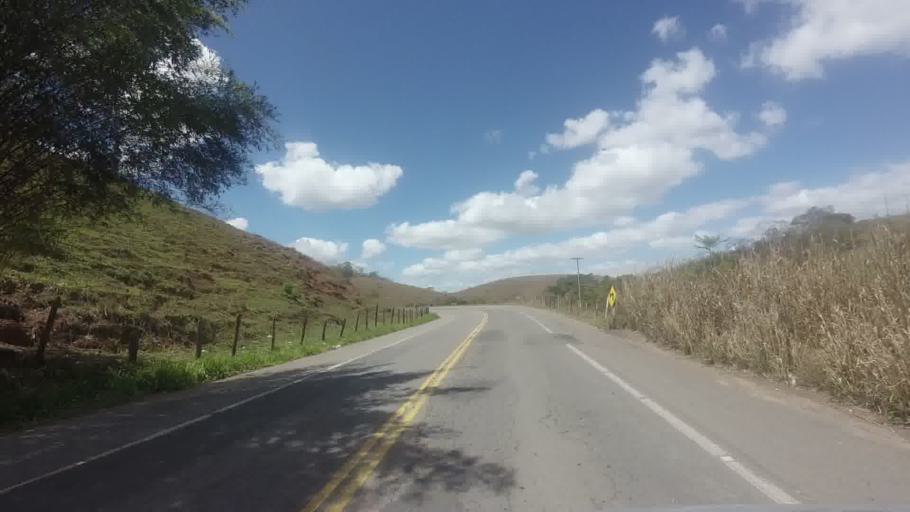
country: BR
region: Rio de Janeiro
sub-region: Santo Antonio De Padua
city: Santo Antonio de Padua
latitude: -21.6573
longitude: -42.3228
